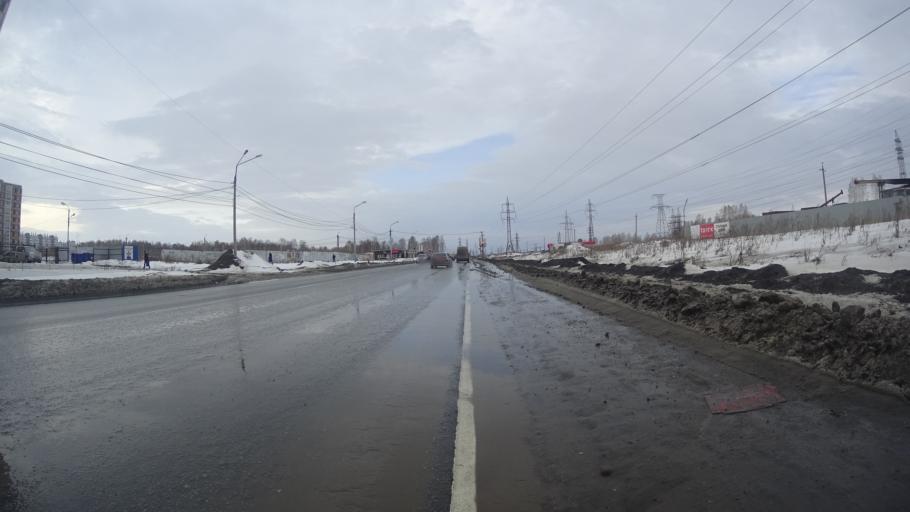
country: RU
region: Chelyabinsk
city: Roshchino
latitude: 55.2197
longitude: 61.2980
